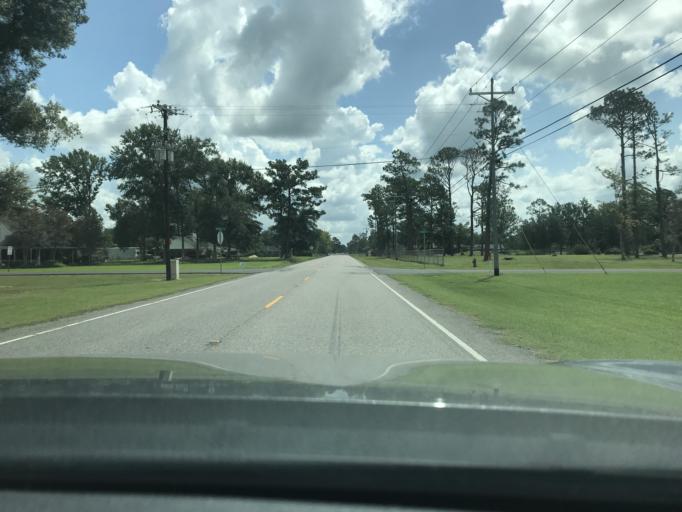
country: US
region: Louisiana
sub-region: Calcasieu Parish
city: Moss Bluff
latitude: 30.3447
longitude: -93.2240
